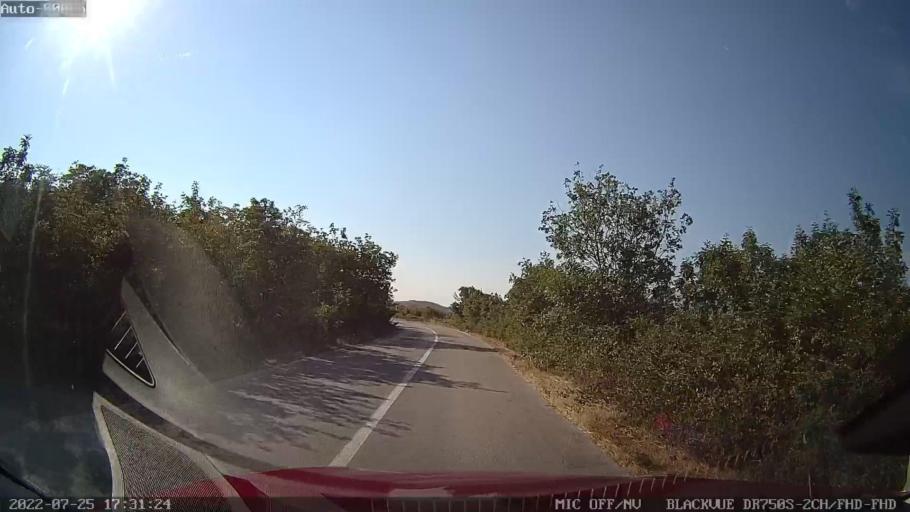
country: HR
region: Zadarska
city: Posedarje
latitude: 44.1702
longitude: 15.4999
